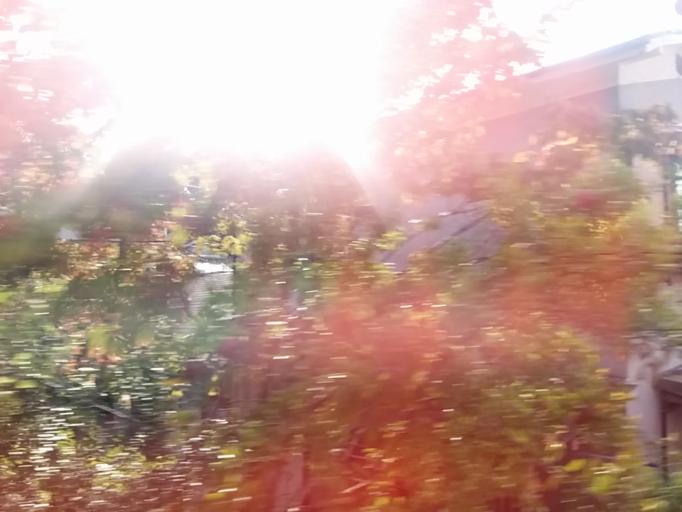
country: JP
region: Nara
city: Nara-shi
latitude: 34.7029
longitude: 135.7867
